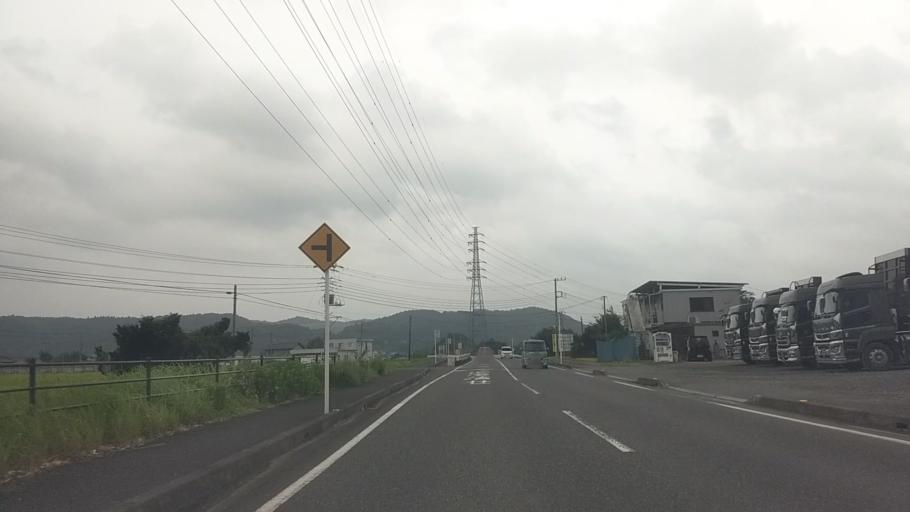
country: JP
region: Chiba
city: Kisarazu
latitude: 35.3117
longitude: 140.0601
